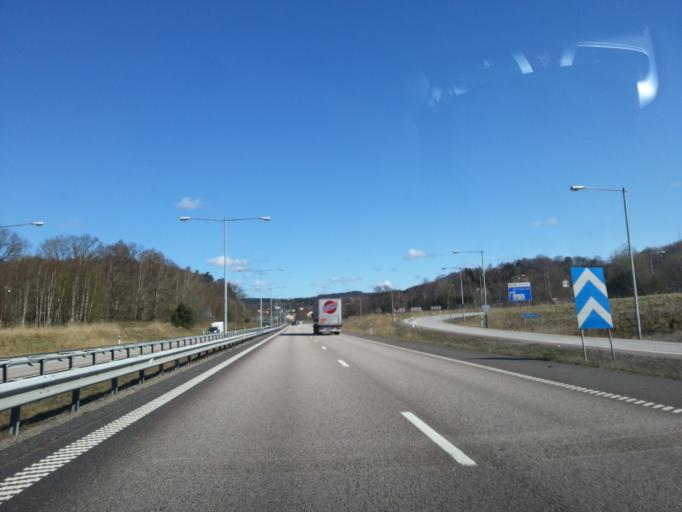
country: SE
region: Vaestra Goetaland
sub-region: Uddevalla Kommun
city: Ljungskile
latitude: 58.2134
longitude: 11.9151
